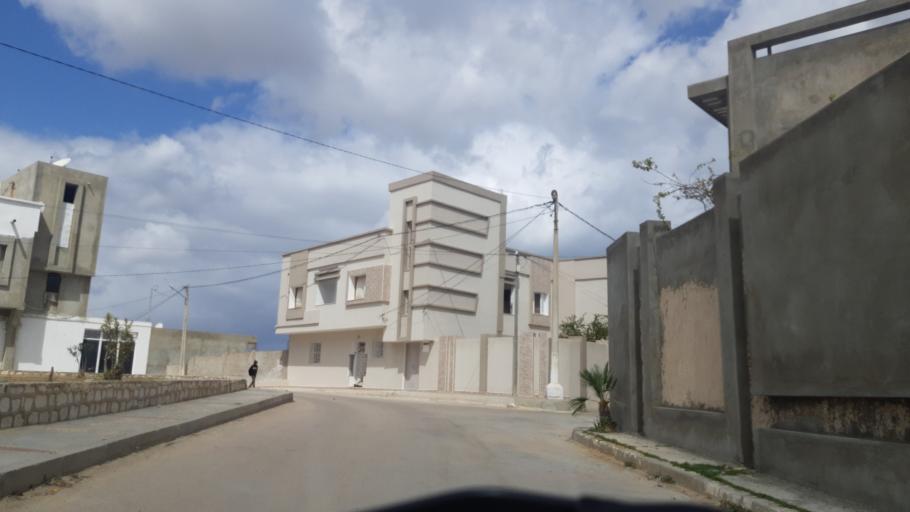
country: TN
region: Susah
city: Akouda
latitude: 35.8624
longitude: 10.5418
